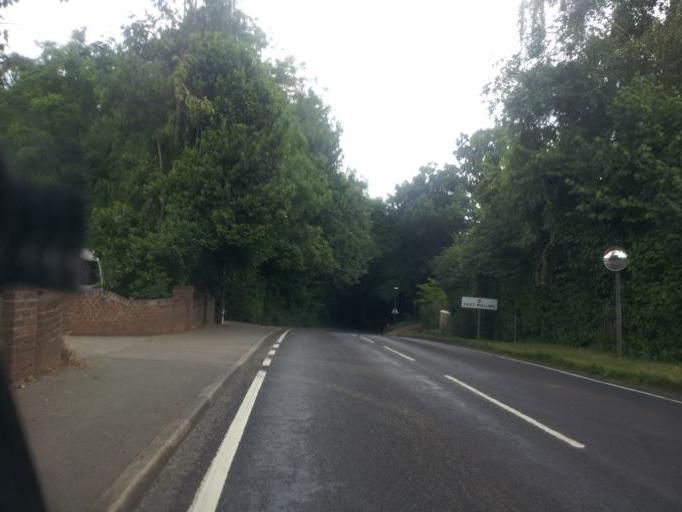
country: GB
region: England
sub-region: Kent
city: Larkfield
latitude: 51.2766
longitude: 0.4348
